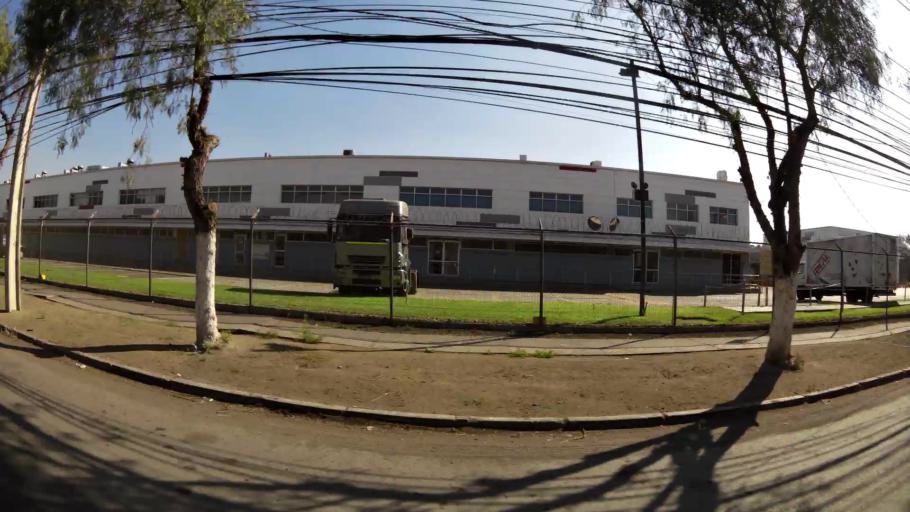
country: CL
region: Santiago Metropolitan
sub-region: Provincia de Chacabuco
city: Chicureo Abajo
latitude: -33.3289
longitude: -70.7239
